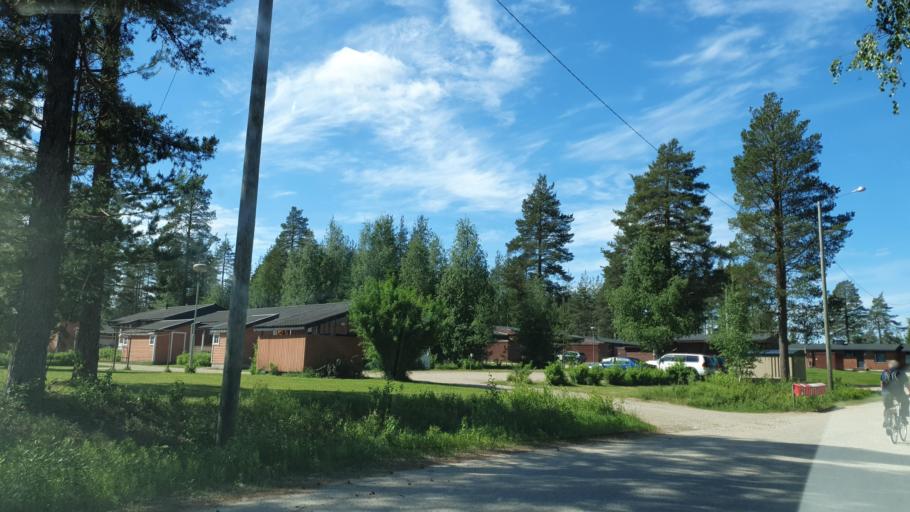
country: FI
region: Kainuu
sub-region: Kehys-Kainuu
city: Hyrynsalmi
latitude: 64.6810
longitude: 28.4672
